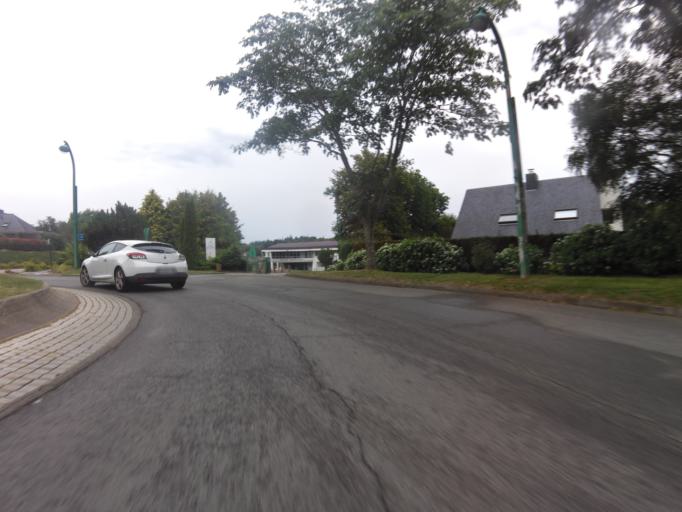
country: FR
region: Brittany
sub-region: Departement du Morbihan
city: Saint-Ave
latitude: 47.6934
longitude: -2.7402
